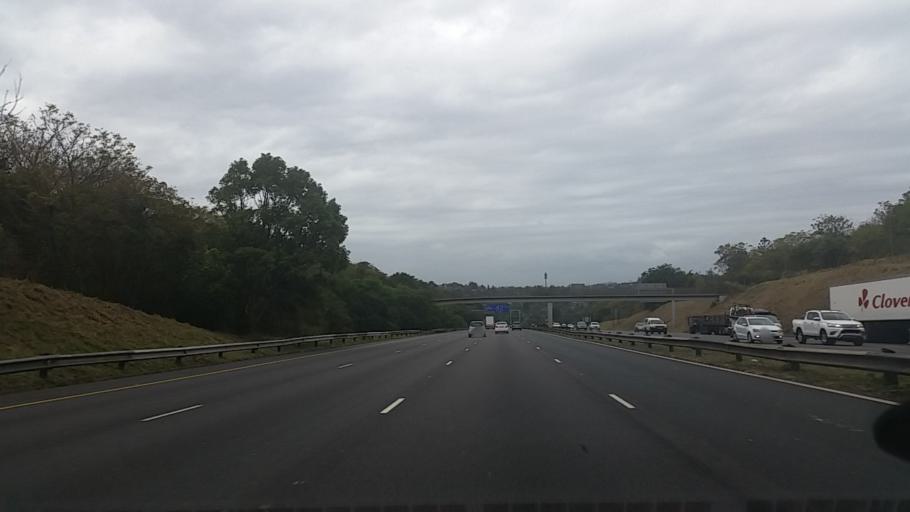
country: ZA
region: KwaZulu-Natal
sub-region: eThekwini Metropolitan Municipality
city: Berea
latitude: -29.8433
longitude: 30.9436
